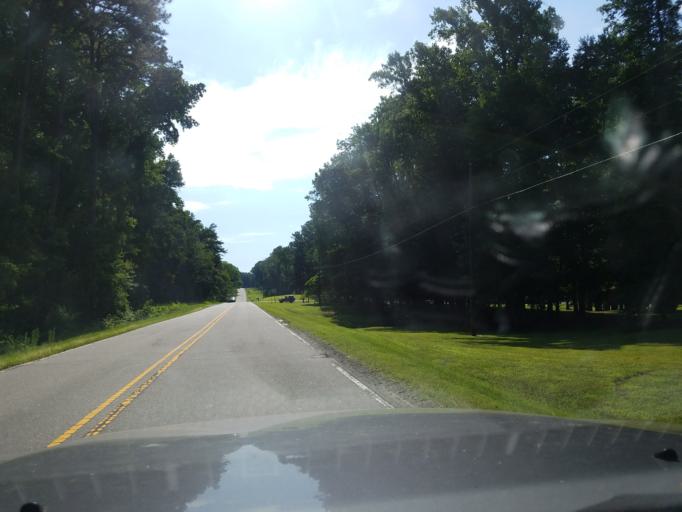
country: US
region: North Carolina
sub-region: Granville County
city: Oxford
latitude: 36.3148
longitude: -78.5224
